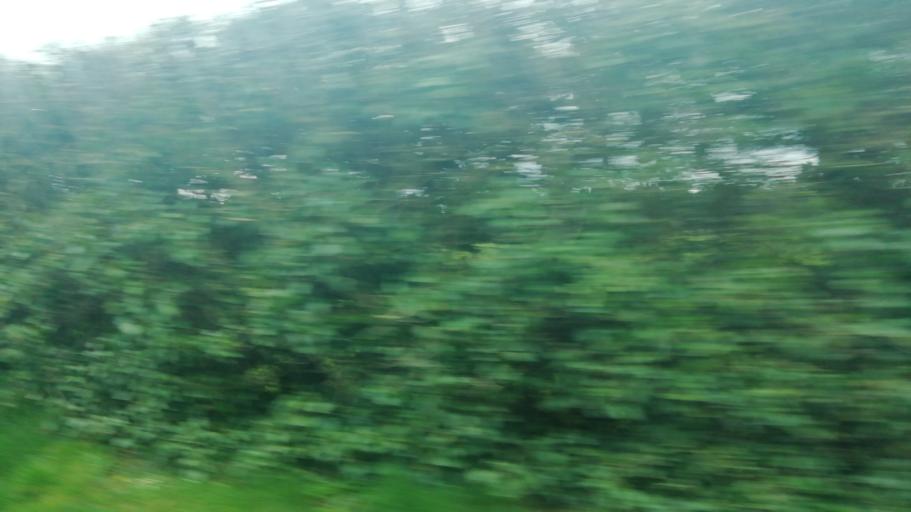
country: IE
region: Leinster
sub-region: Kildare
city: Celbridge
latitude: 53.3602
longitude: -6.5651
